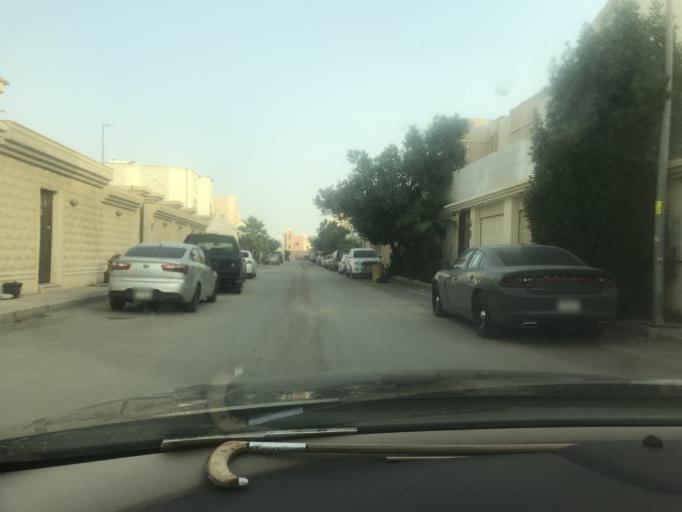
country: SA
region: Ar Riyad
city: Riyadh
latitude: 24.7457
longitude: 46.7791
